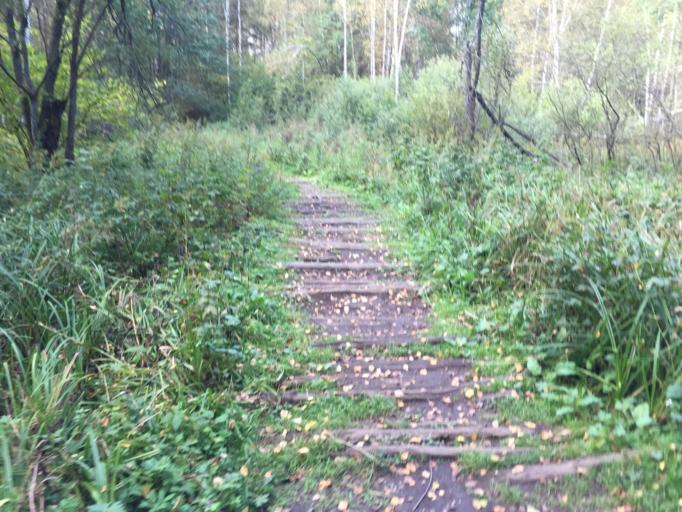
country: RU
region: Moscow
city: Babushkin
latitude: 55.8693
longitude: 37.7351
